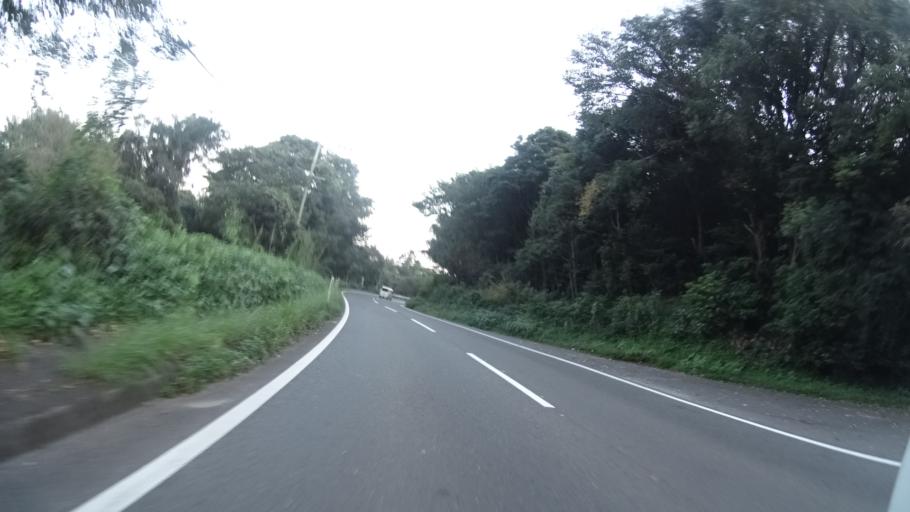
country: JP
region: Oita
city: Beppu
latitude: 33.3197
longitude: 131.4581
